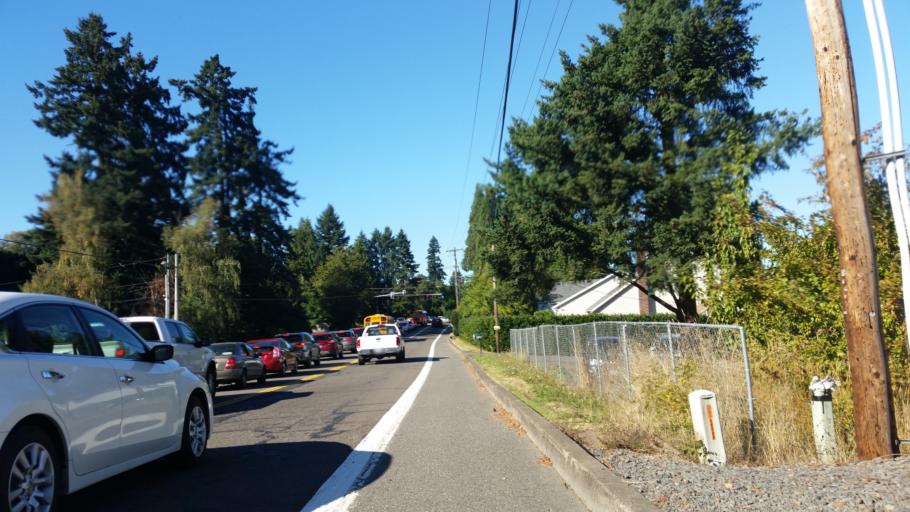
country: US
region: Oregon
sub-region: Washington County
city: Tigard
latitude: 45.4174
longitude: -122.7651
